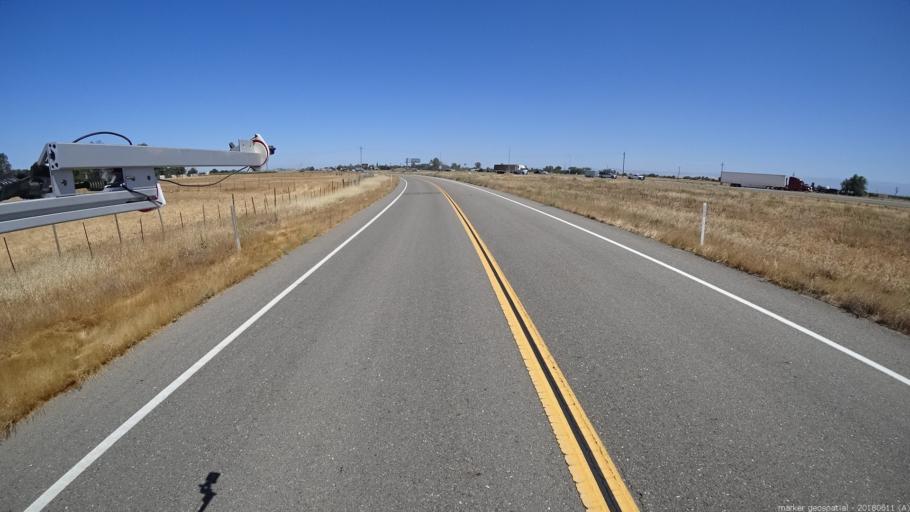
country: US
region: California
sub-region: Madera County
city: Fairmead
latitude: 37.0671
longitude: -120.1904
